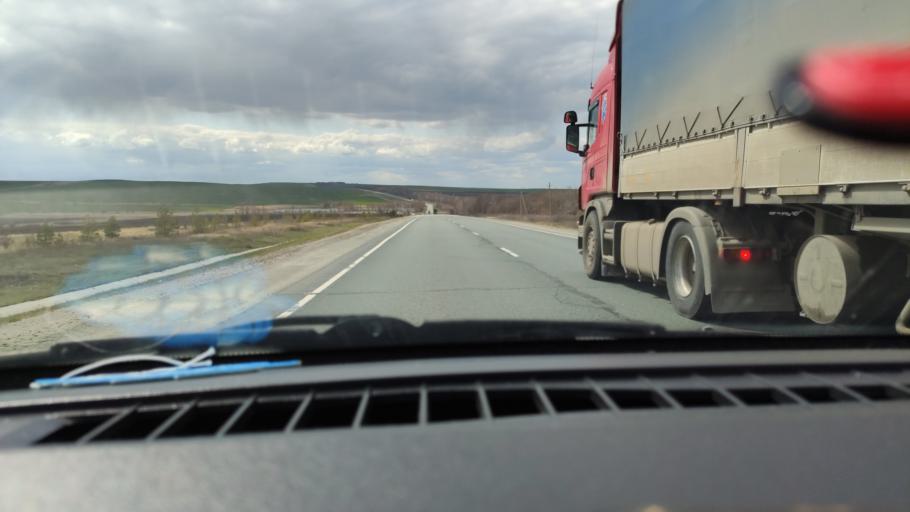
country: RU
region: Saratov
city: Alekseyevka
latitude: 52.2511
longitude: 47.9128
